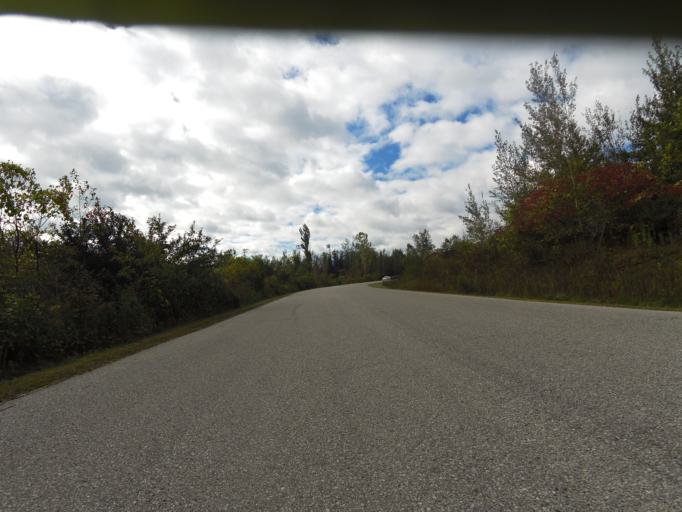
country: CA
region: Ontario
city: Scarborough
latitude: 43.7620
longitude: -79.1599
